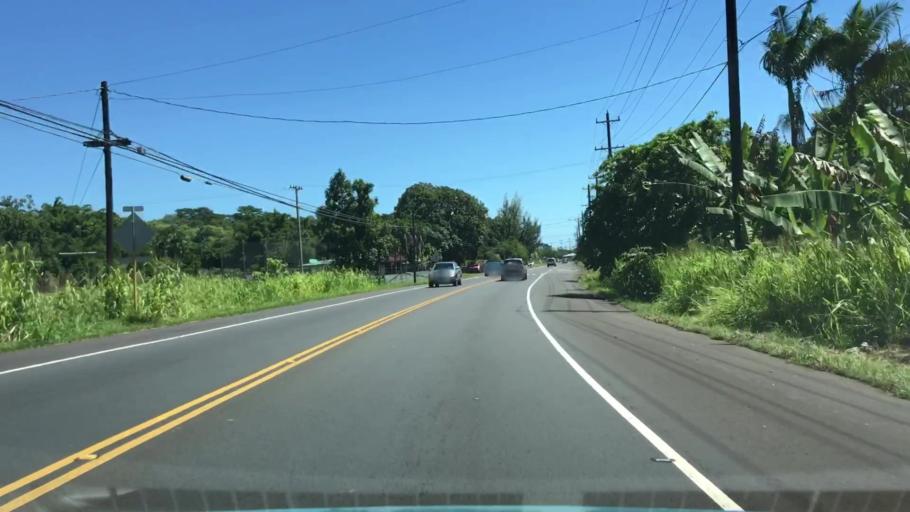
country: US
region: Hawaii
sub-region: Hawaii County
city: Kurtistown
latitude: 19.5907
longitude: -155.0602
